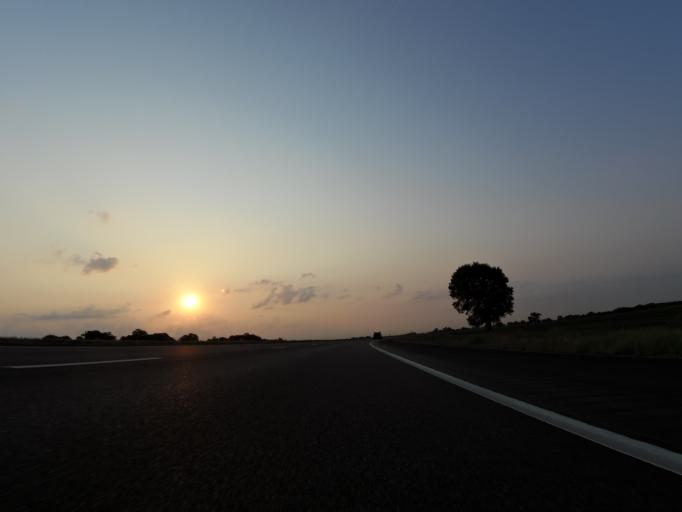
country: US
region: Kansas
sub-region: Sedgwick County
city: Colwich
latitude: 37.8235
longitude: -97.5157
